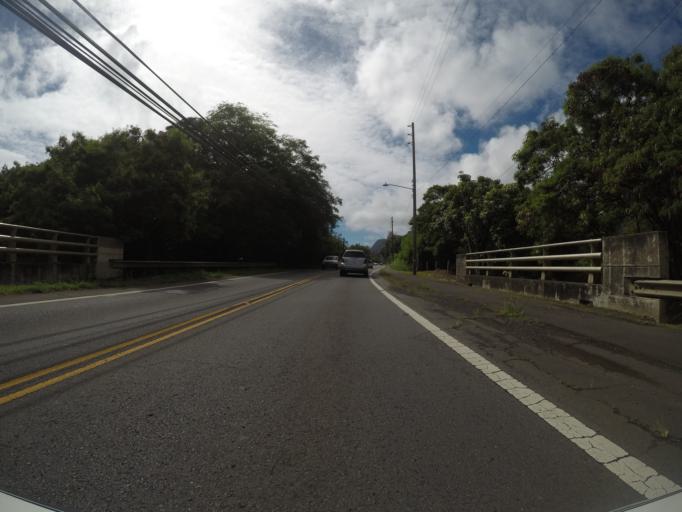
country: US
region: Hawaii
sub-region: Honolulu County
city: Waimanalo
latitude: 21.3462
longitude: -157.7115
